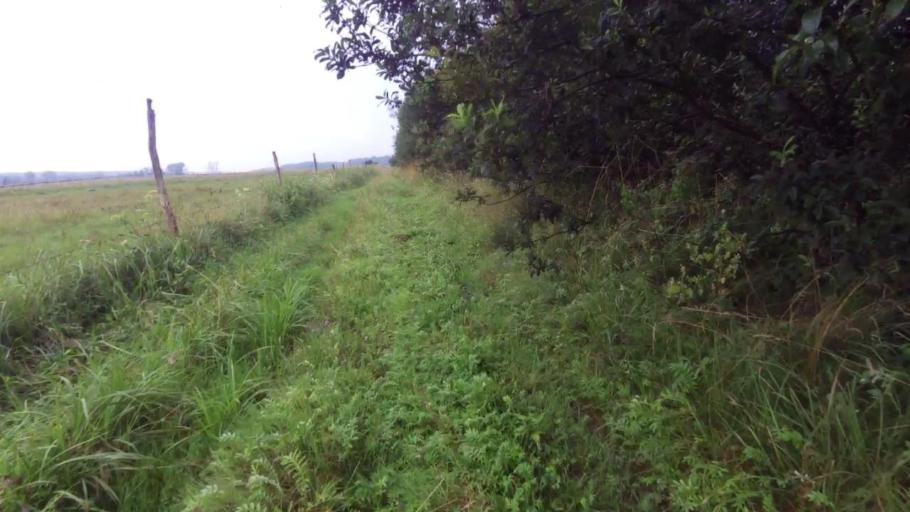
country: PL
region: West Pomeranian Voivodeship
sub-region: Powiat stargardzki
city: Suchan
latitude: 53.2508
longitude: 15.4003
